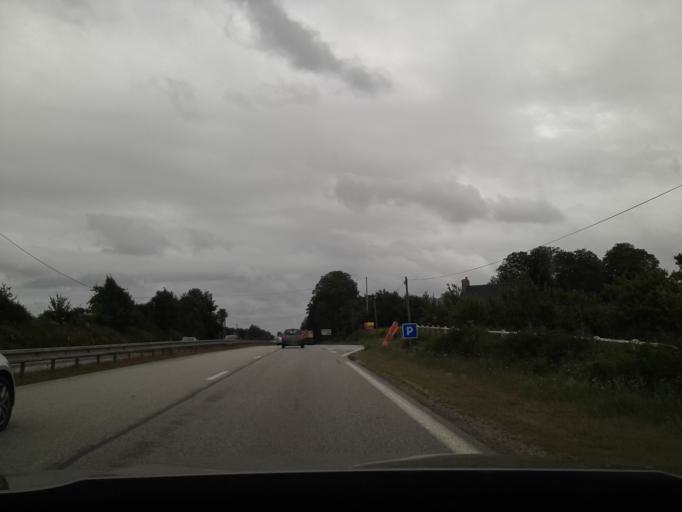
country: FR
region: Lower Normandy
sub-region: Departement de la Manche
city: Valognes
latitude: 49.5273
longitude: -1.5139
